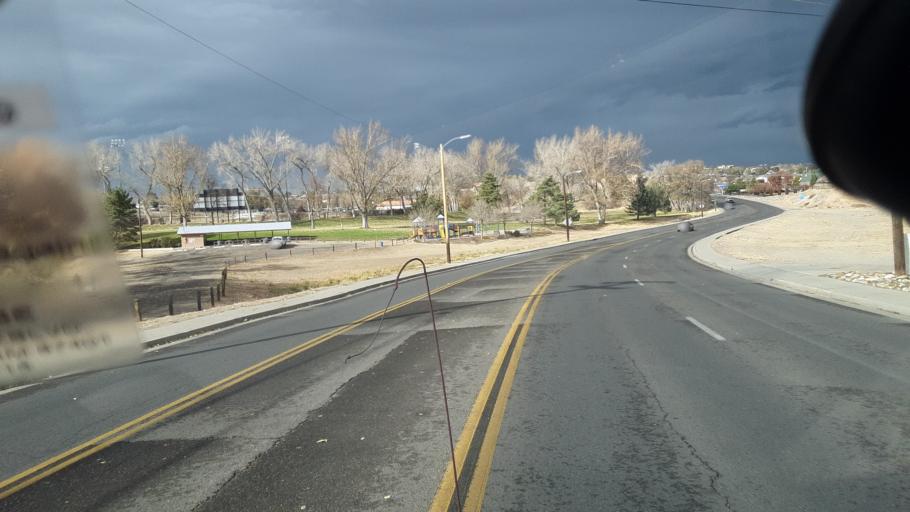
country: US
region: New Mexico
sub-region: San Juan County
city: Farmington
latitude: 36.7520
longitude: -108.1977
